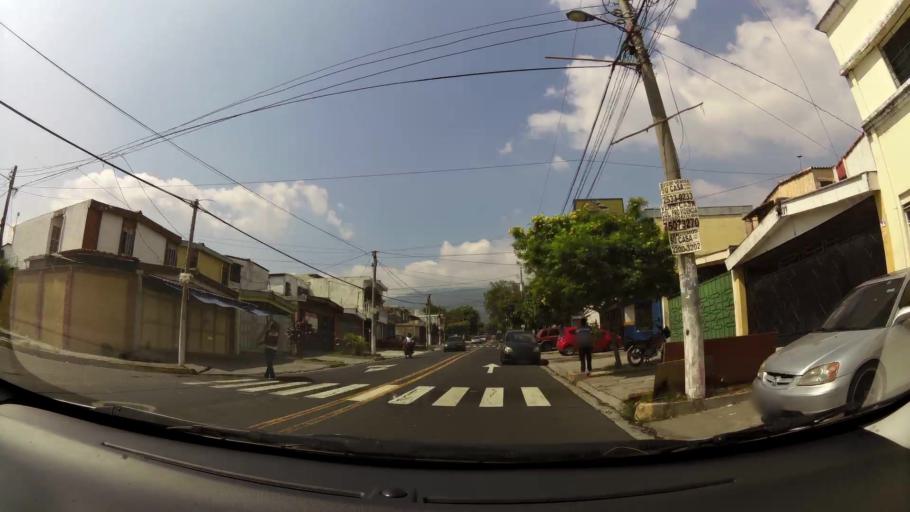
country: SV
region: San Salvador
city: Mejicanos
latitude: 13.7141
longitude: -89.2199
